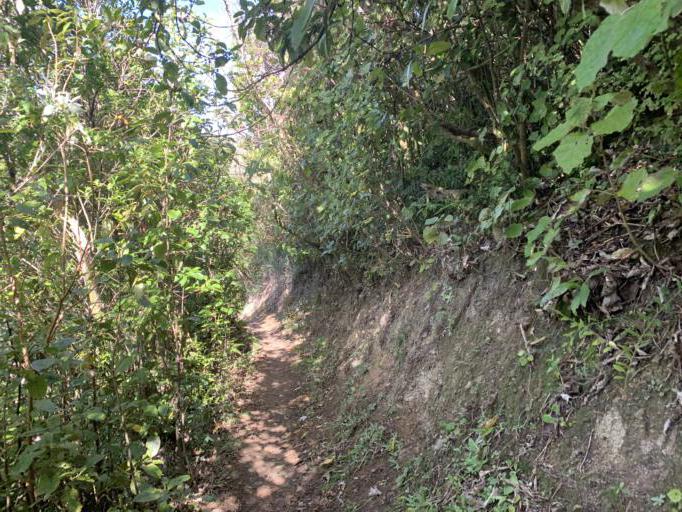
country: NZ
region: Wellington
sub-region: Wellington City
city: Brooklyn
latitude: -41.2995
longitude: 174.7540
